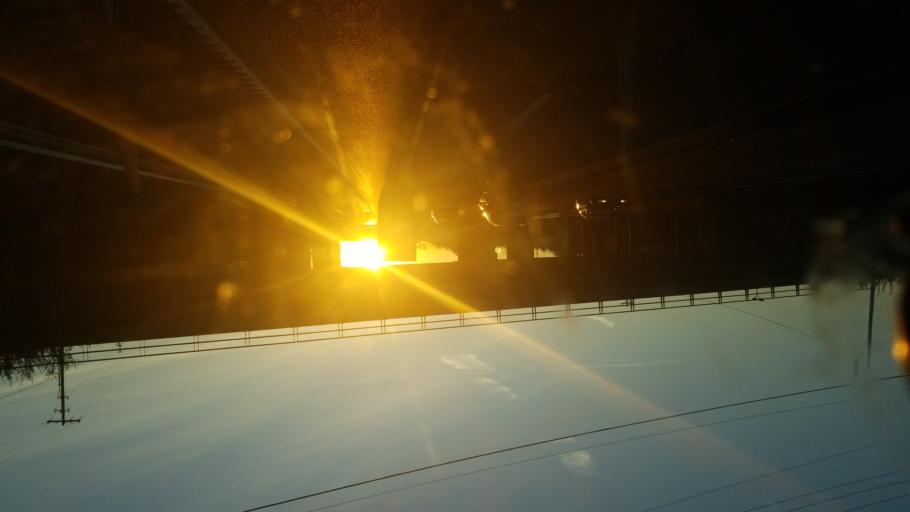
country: US
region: Missouri
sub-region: Boone County
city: Columbia
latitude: 38.9674
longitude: -92.3091
